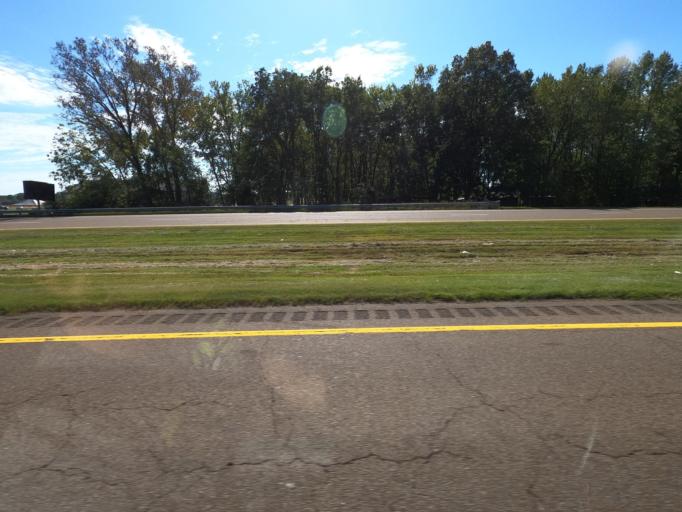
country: US
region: Tennessee
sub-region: Dyer County
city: Dyersburg
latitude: 36.0677
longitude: -89.3609
